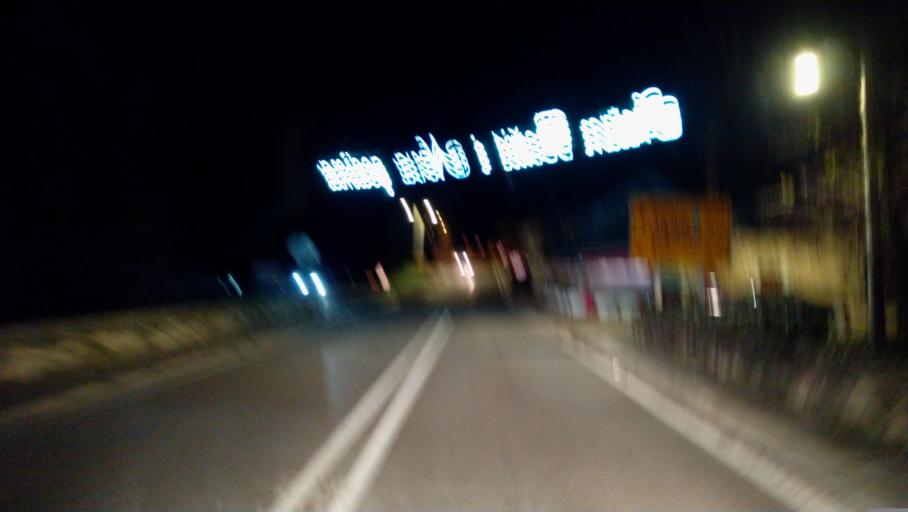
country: HR
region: Sibensko-Kniniska
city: Drnis
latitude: 43.8567
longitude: 16.1592
